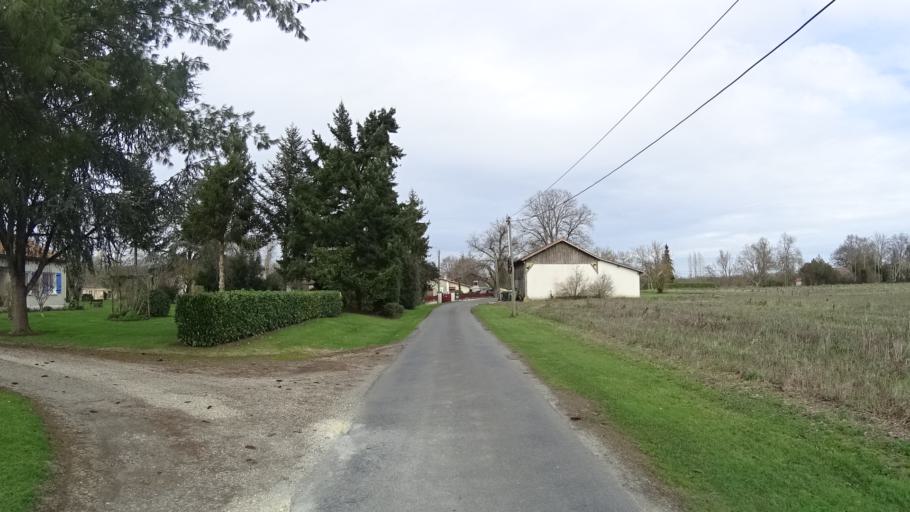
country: FR
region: Aquitaine
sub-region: Departement de la Dordogne
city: Saint-Aulaye
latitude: 45.2241
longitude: 0.1466
